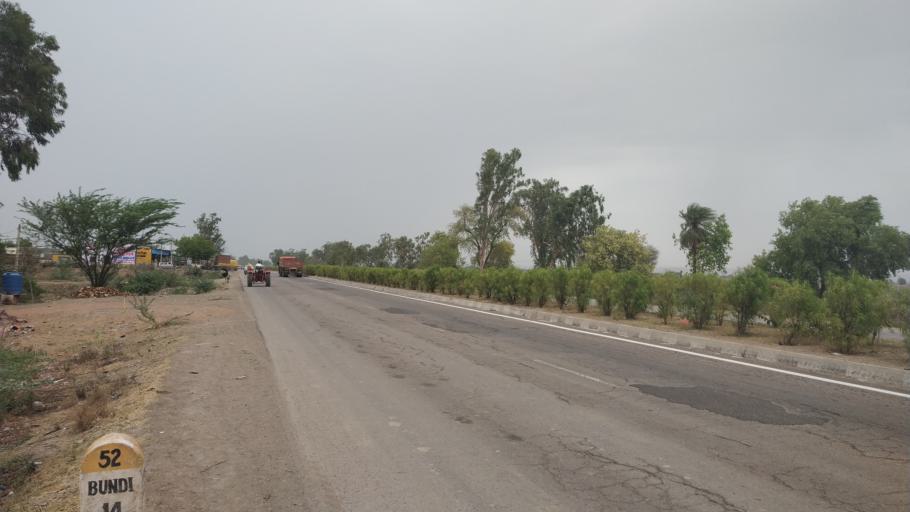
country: IN
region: Rajasthan
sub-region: Bundi
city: Bundi
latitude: 25.3298
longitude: 75.7137
